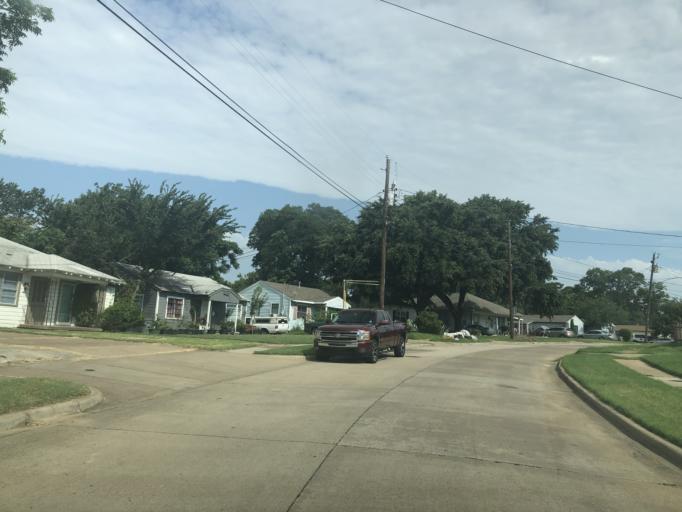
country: US
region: Texas
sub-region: Dallas County
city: Dallas
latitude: 32.8146
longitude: -96.8528
